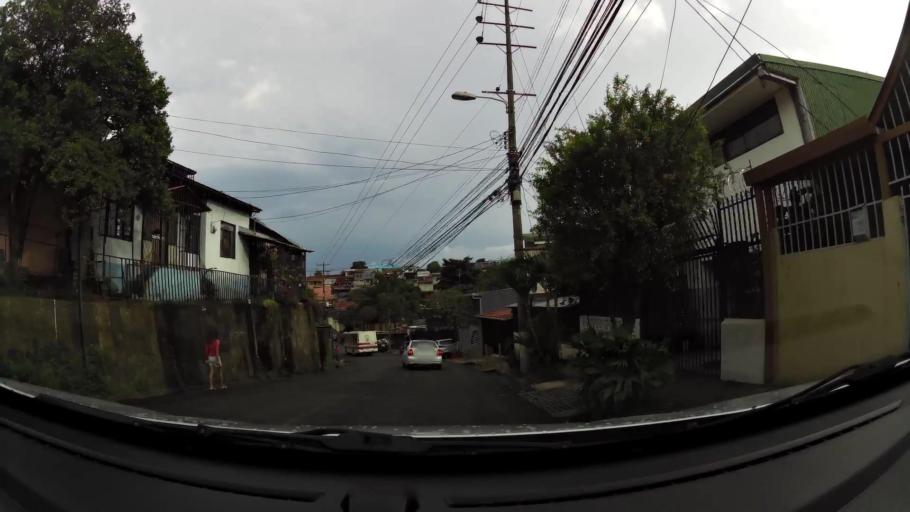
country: CR
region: San Jose
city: San Jose
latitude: 9.9391
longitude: -84.0929
